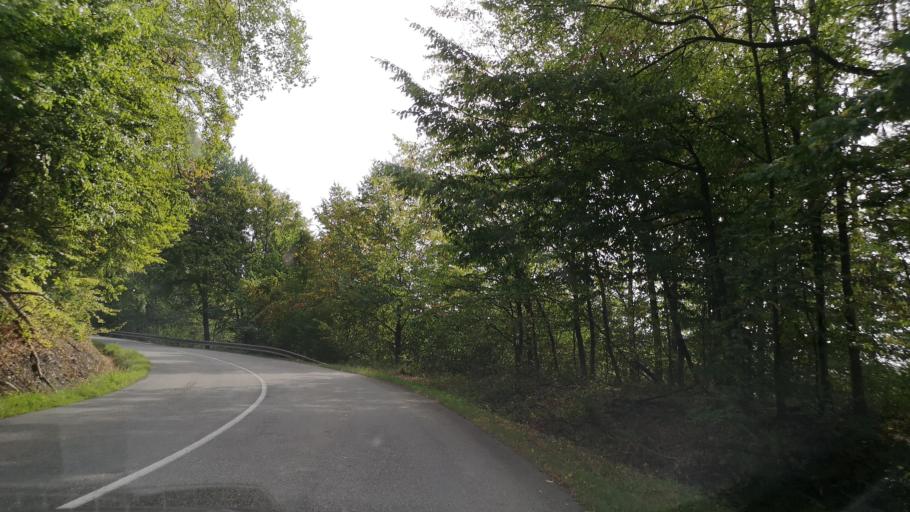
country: SK
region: Banskobystricky
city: Tisovec
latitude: 48.5760
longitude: 19.9866
